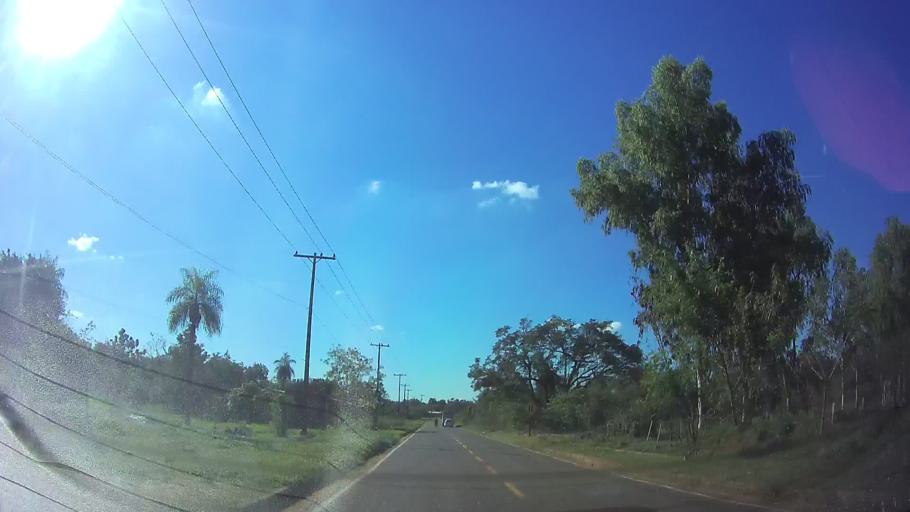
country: PY
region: Central
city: Limpio
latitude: -25.1945
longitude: -57.4768
